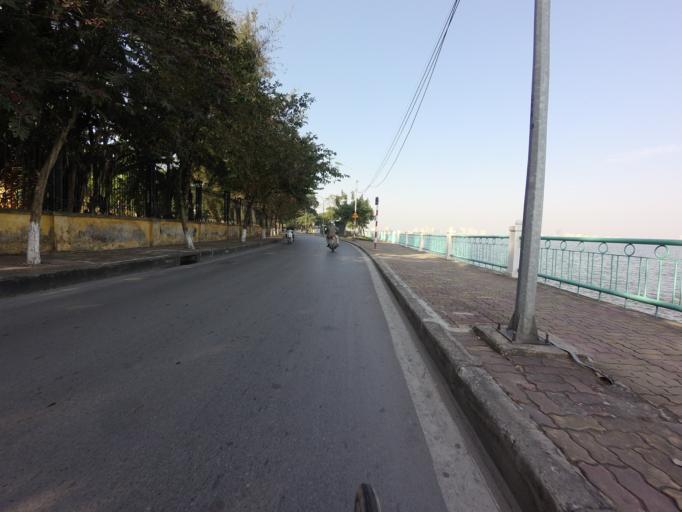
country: VN
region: Ha Noi
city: Hanoi
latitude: 21.0438
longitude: 105.8325
